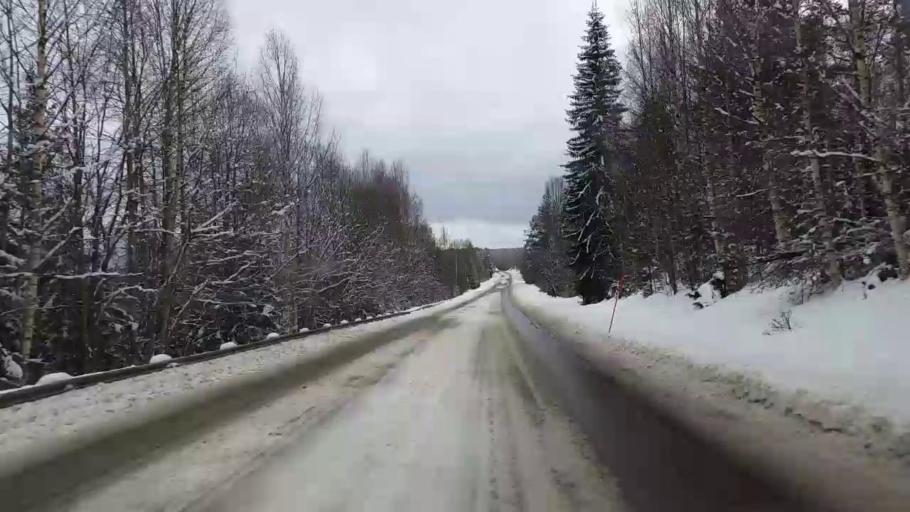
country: SE
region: Vaesternorrland
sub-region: Ange Kommun
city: Ange
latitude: 62.0769
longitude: 15.1007
